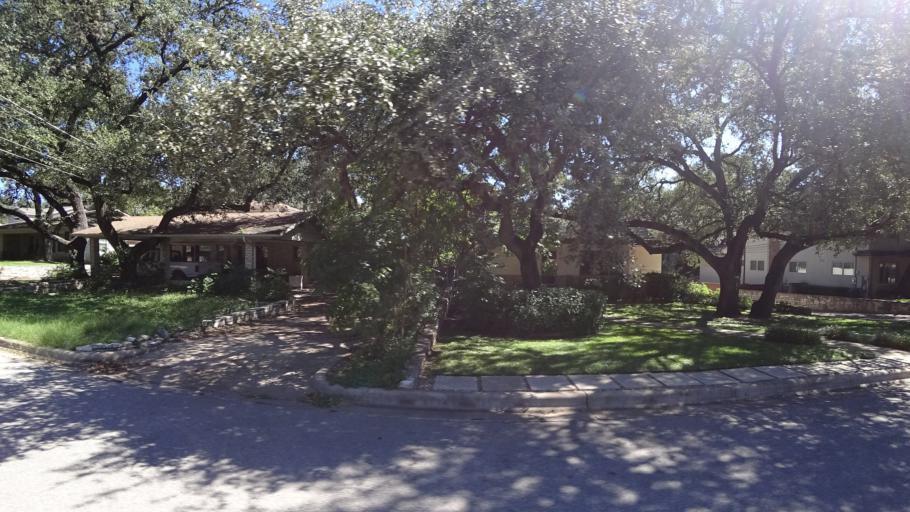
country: US
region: Texas
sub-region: Travis County
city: Austin
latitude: 30.2437
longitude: -97.7385
